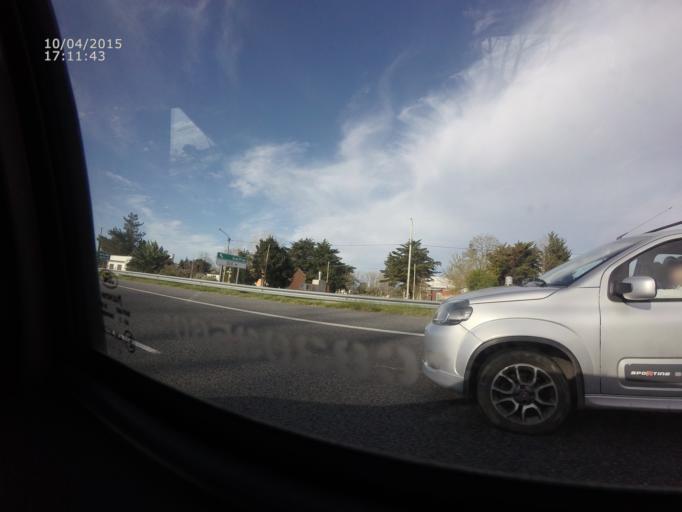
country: AR
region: Buenos Aires
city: Coronel Vidal
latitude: -37.2781
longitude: -57.7652
